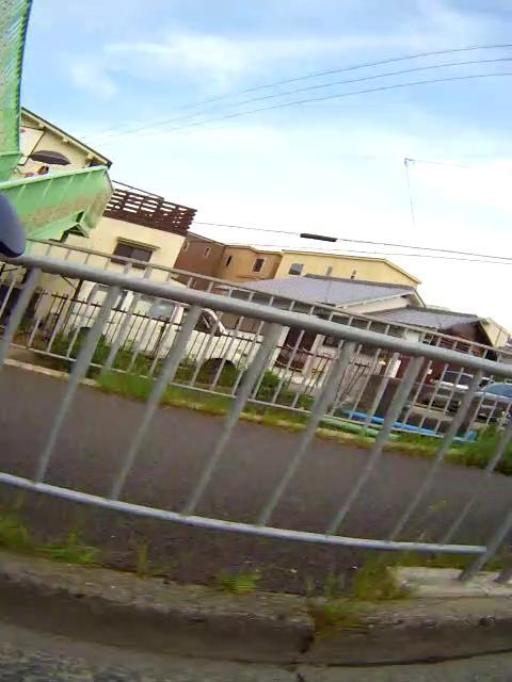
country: JP
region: Osaka
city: Toyonaka
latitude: 34.7870
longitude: 135.4774
